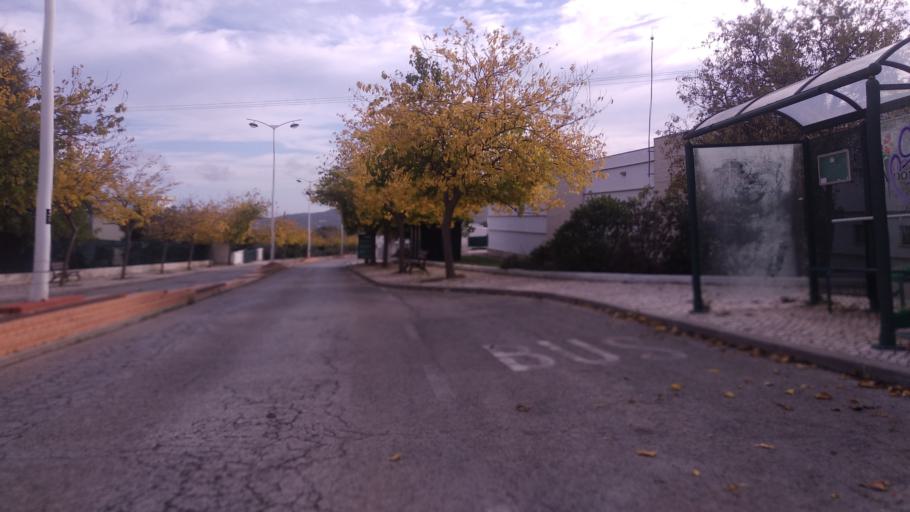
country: PT
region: Faro
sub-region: Sao Bras de Alportel
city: Sao Bras de Alportel
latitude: 37.1501
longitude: -7.8934
